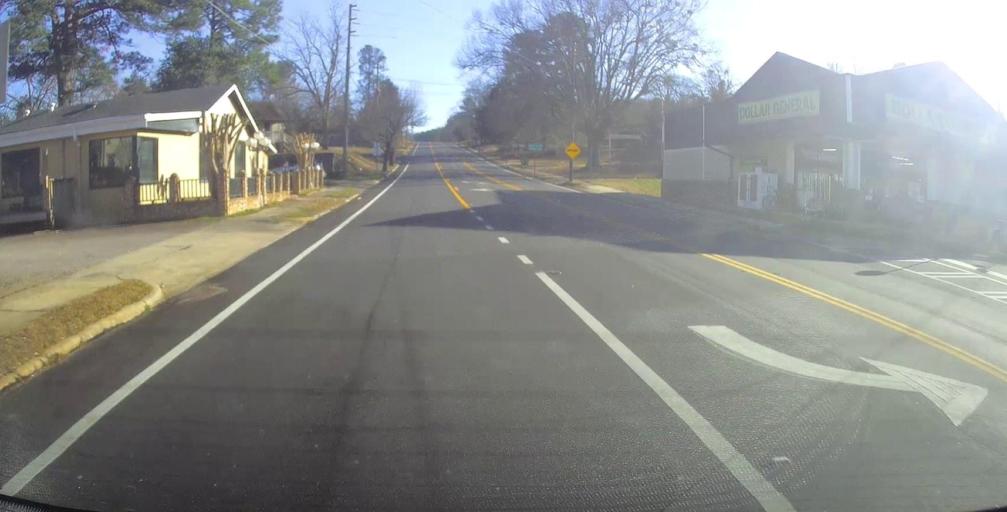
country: US
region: Georgia
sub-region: Meriwether County
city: Manchester
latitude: 32.8899
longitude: -84.6810
